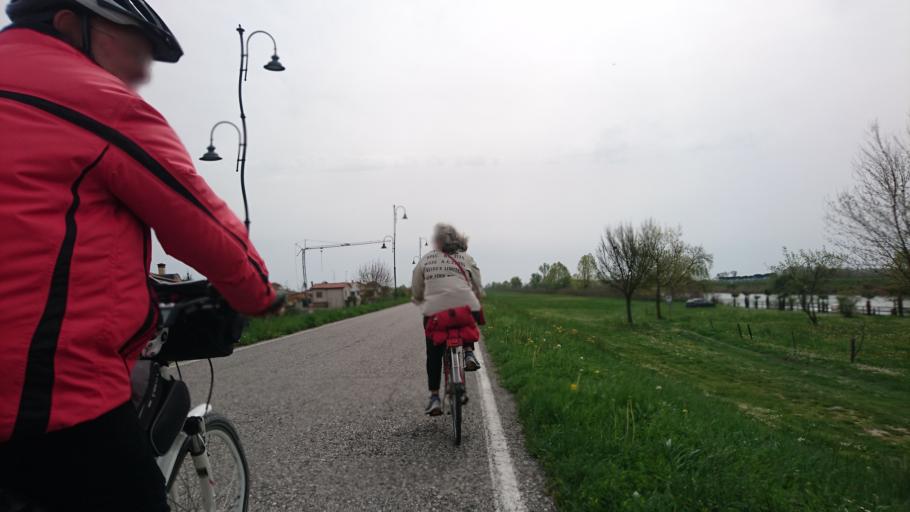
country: IT
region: Veneto
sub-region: Provincia di Venezia
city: La Salute di Livenza
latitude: 45.6544
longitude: 12.8050
